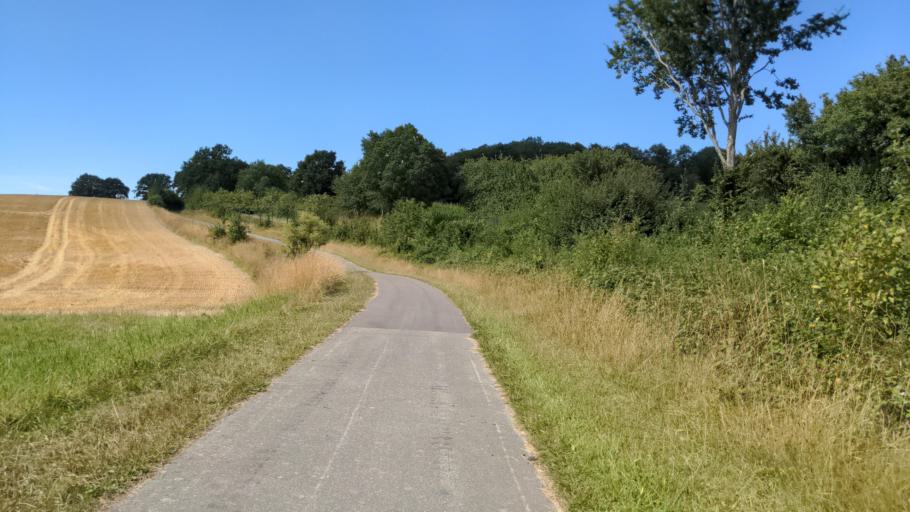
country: DE
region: Schleswig-Holstein
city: Malente
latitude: 54.1845
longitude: 10.5307
